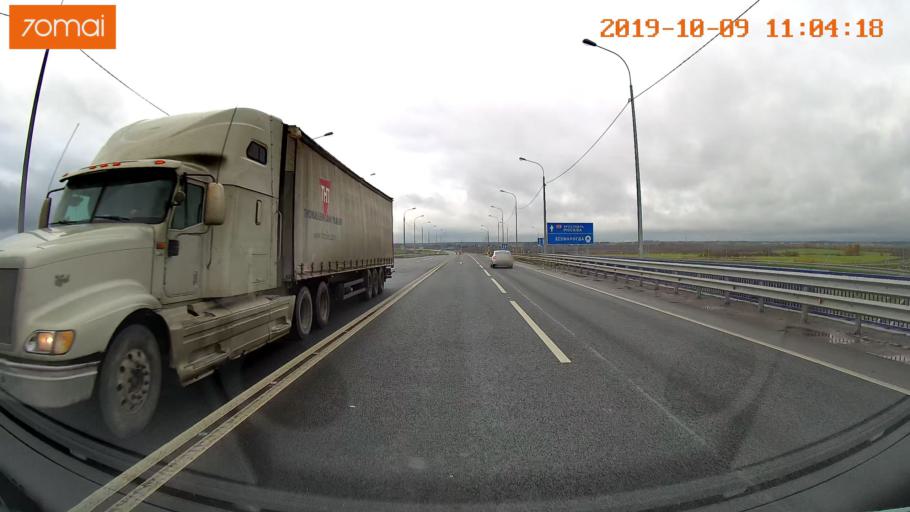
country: RU
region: Vologda
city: Vologda
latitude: 59.2135
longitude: 39.7688
